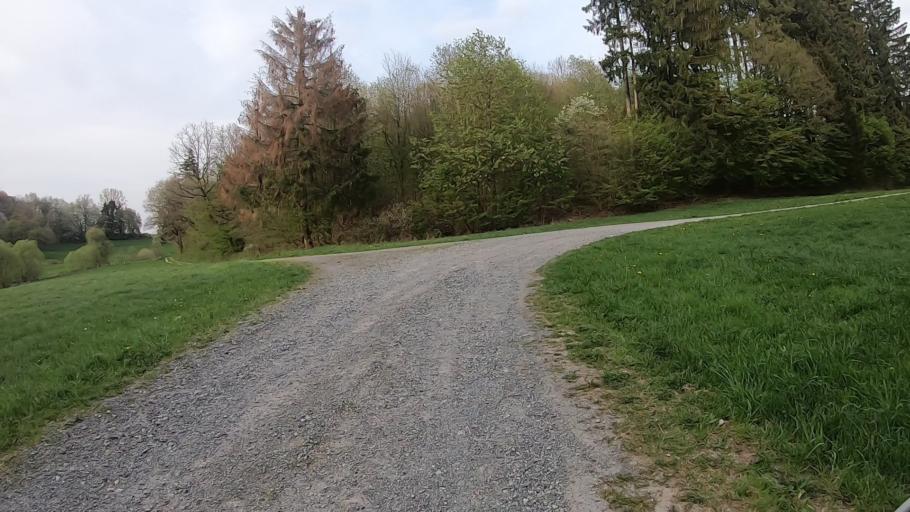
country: DE
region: Rheinland-Pfalz
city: Niedersayn
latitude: 50.5408
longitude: 7.8220
